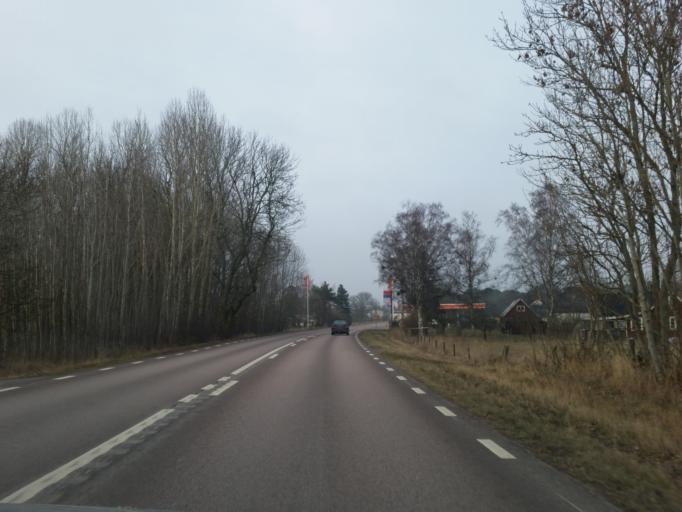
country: SE
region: Kalmar
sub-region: Borgholms Kommun
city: Borgholm
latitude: 57.1599
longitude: 17.0103
